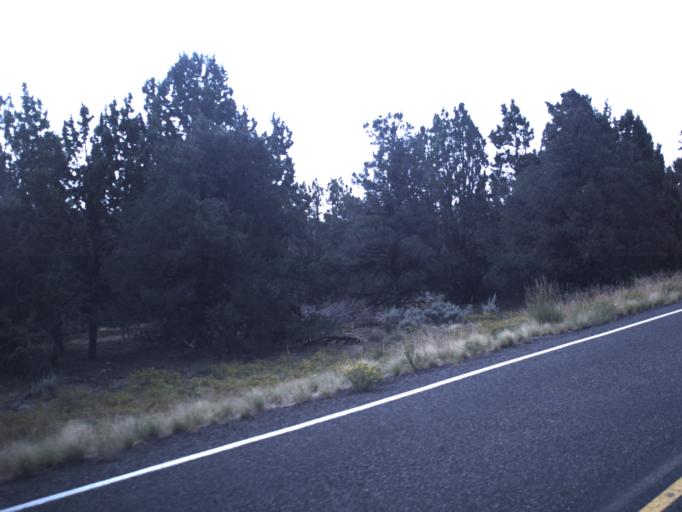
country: US
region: Utah
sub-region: Washington County
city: Hildale
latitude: 37.2585
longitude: -112.7919
